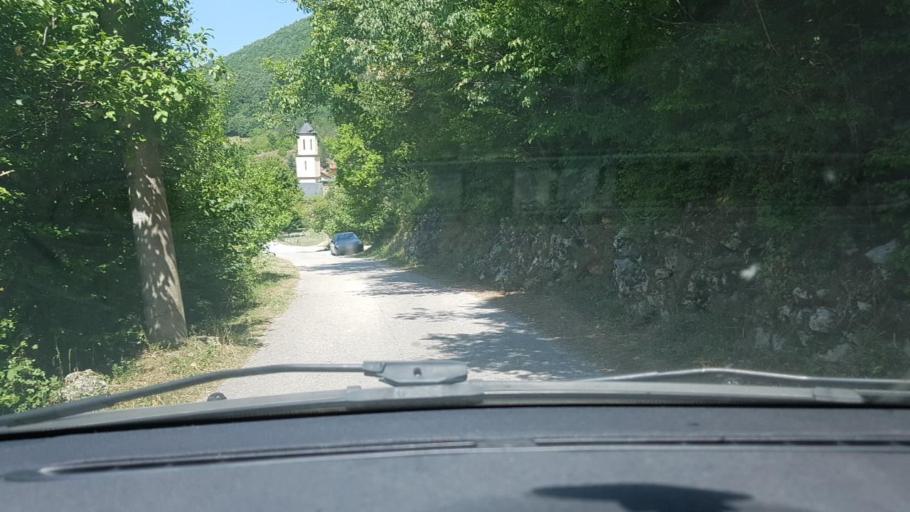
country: BA
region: Federation of Bosnia and Herzegovina
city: Orasac
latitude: 44.4917
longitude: 16.1440
